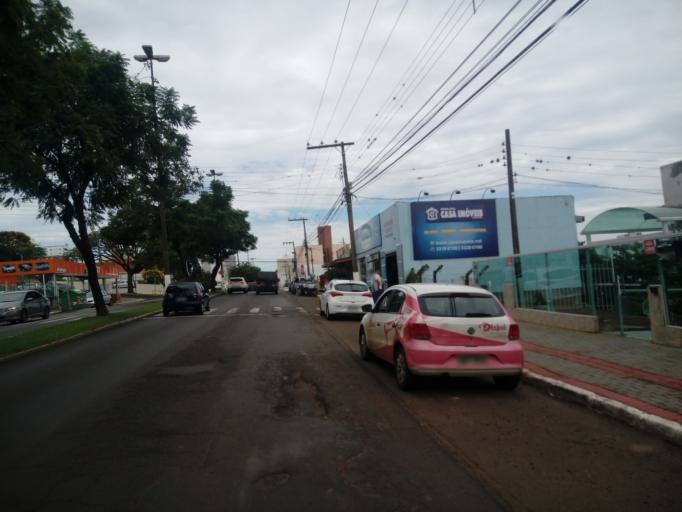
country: BR
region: Santa Catarina
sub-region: Chapeco
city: Chapeco
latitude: -27.0970
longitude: -52.6216
